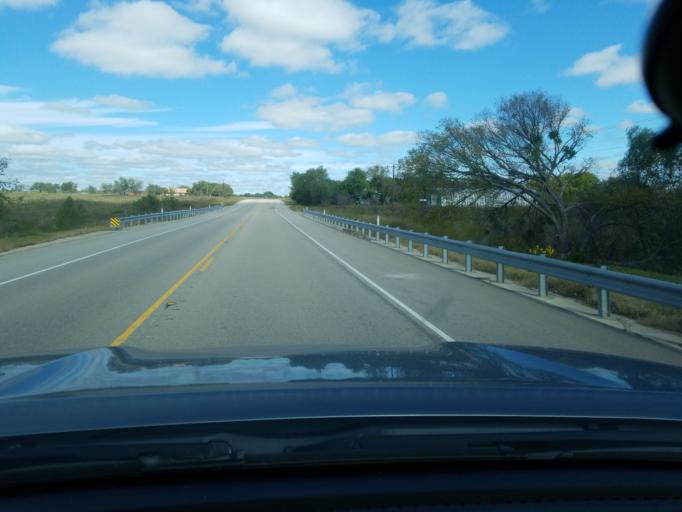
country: US
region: Texas
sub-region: Hamilton County
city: Hamilton
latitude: 31.6430
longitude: -98.1487
